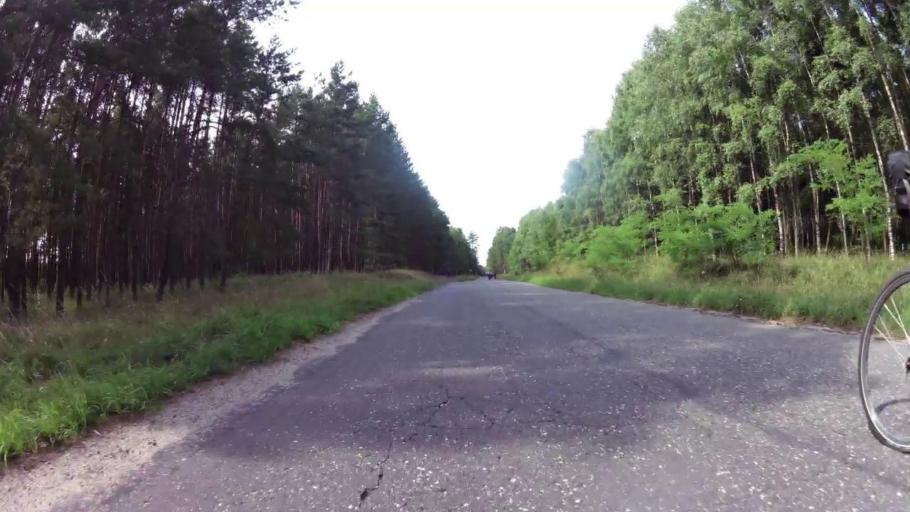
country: PL
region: West Pomeranian Voivodeship
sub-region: Powiat stargardzki
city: Insko
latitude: 53.3817
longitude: 15.5969
